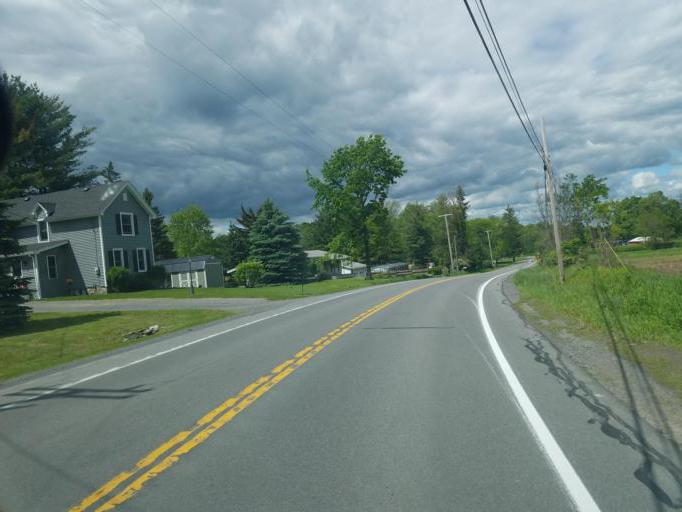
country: US
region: New York
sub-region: Herkimer County
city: Mohawk
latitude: 42.9585
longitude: -75.0162
